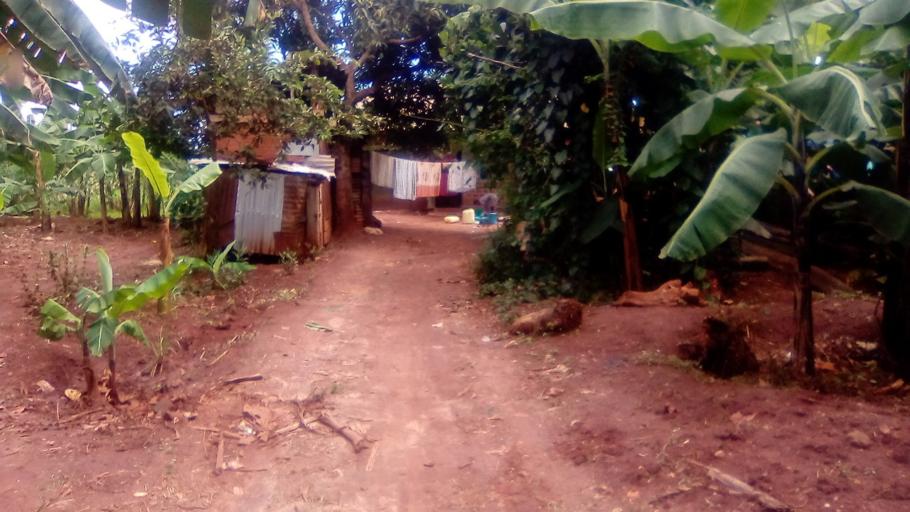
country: UG
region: Central Region
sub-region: Wakiso District
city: Entebbe
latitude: 0.1007
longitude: 32.5277
